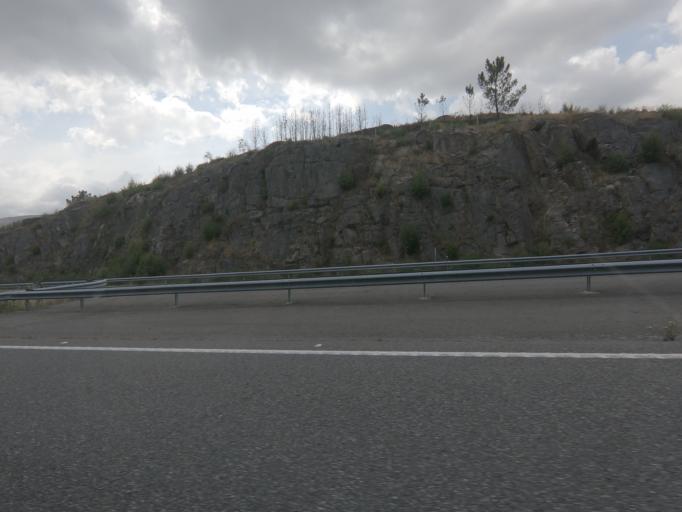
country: ES
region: Galicia
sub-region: Provincia de Ourense
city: Melon
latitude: 42.2721
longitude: -8.2037
